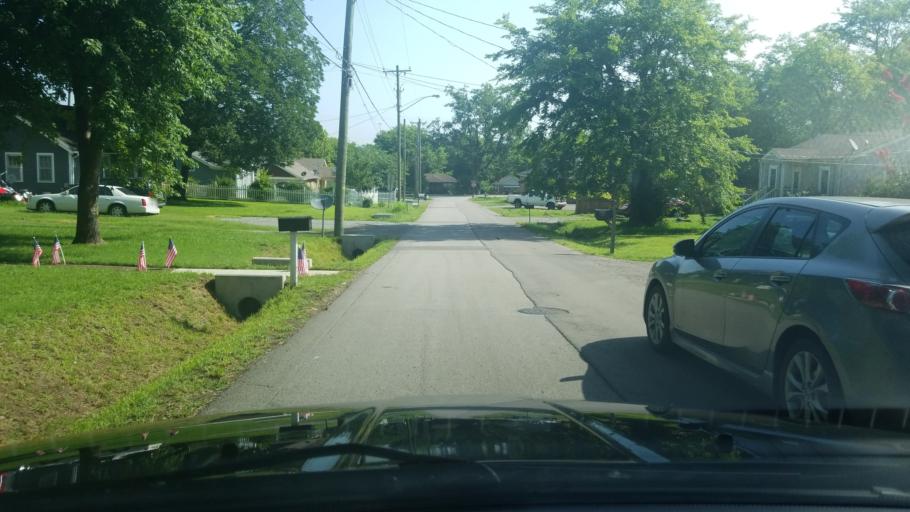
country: US
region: Tennessee
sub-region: Davidson County
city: Belle Meade
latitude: 36.1541
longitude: -86.8619
